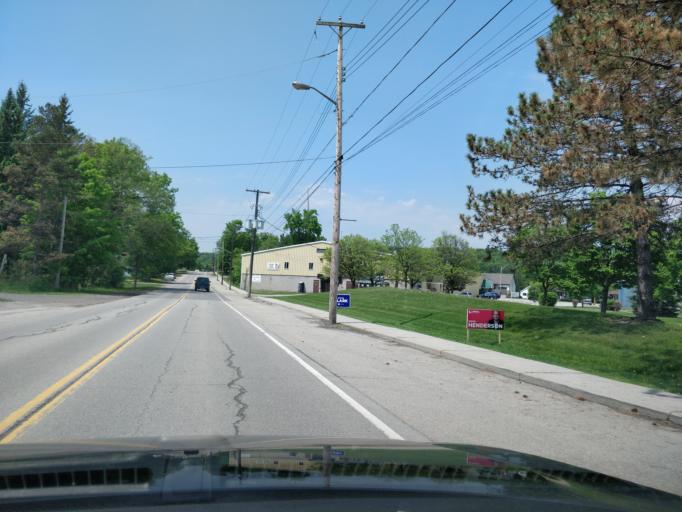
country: CA
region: Ontario
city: Perth
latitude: 44.6764
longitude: -76.4000
